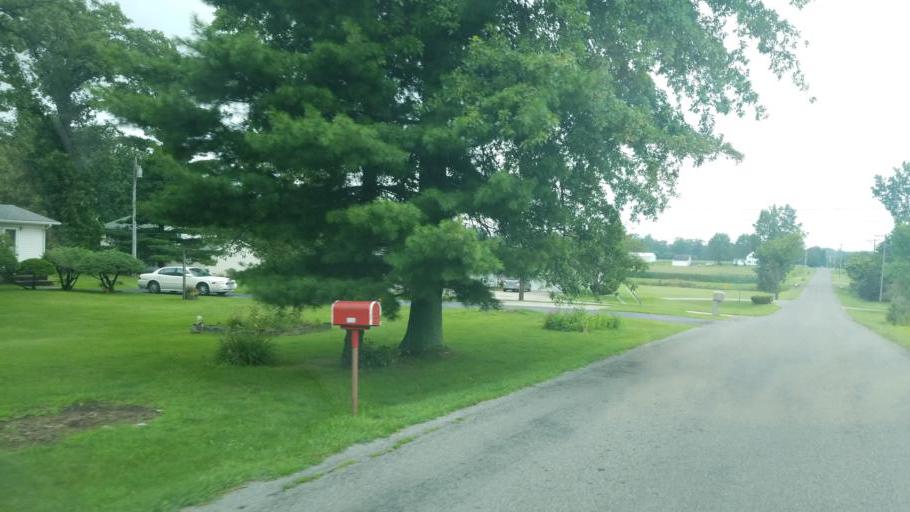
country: US
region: Ohio
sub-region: Logan County
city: Russells Point
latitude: 40.4624
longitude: -83.8573
